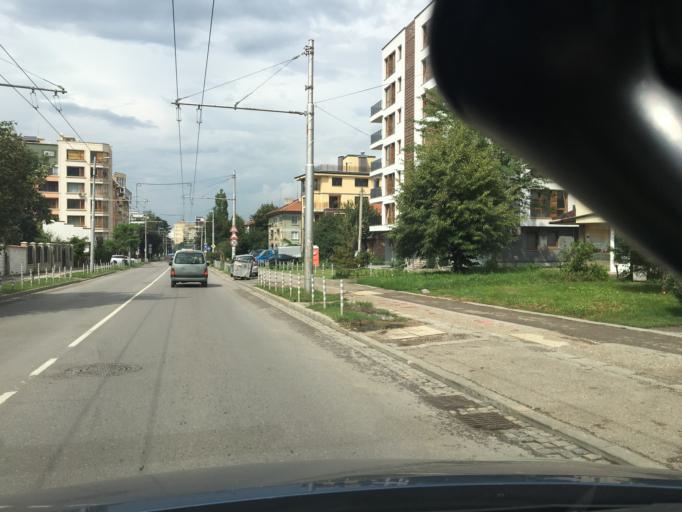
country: BG
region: Sofia-Capital
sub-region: Stolichna Obshtina
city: Sofia
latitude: 42.6621
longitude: 23.2739
